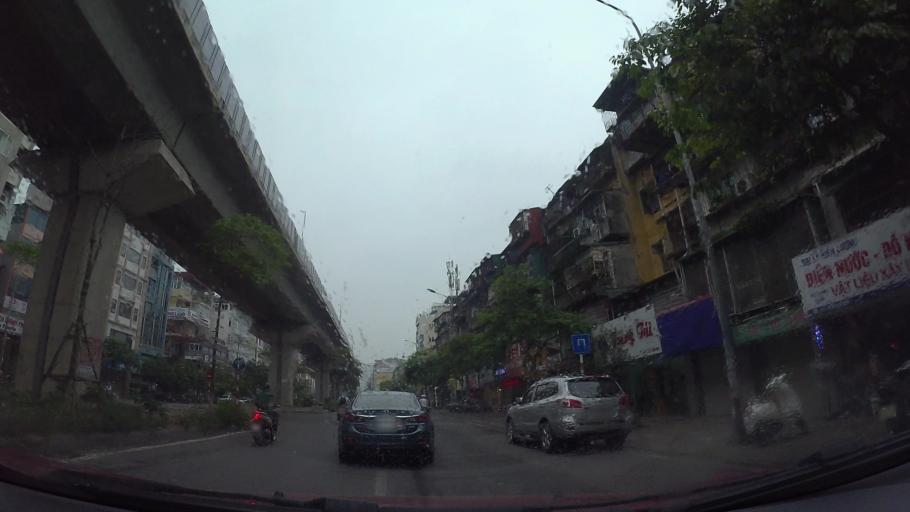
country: VN
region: Ha Noi
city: Dong Da
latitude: 21.0133
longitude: 105.8183
